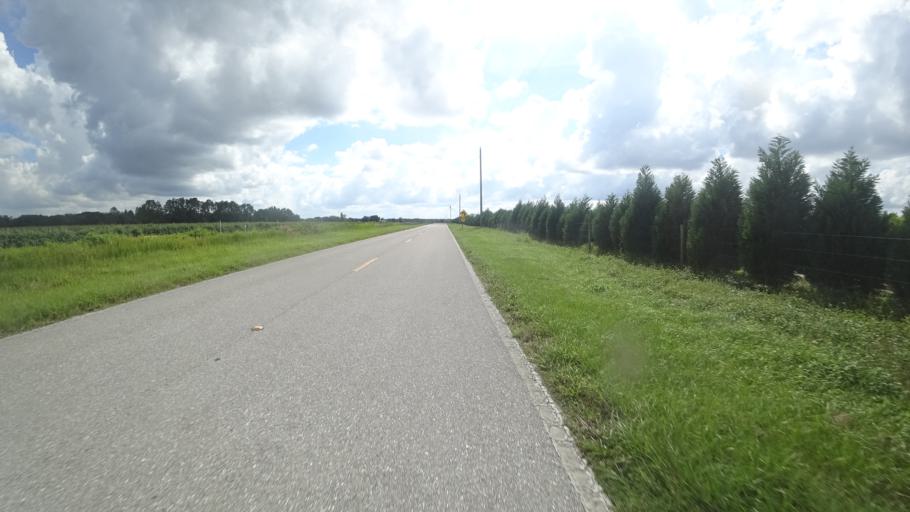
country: US
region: Florida
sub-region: Hillsborough County
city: Wimauma
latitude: 27.6139
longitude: -82.2311
